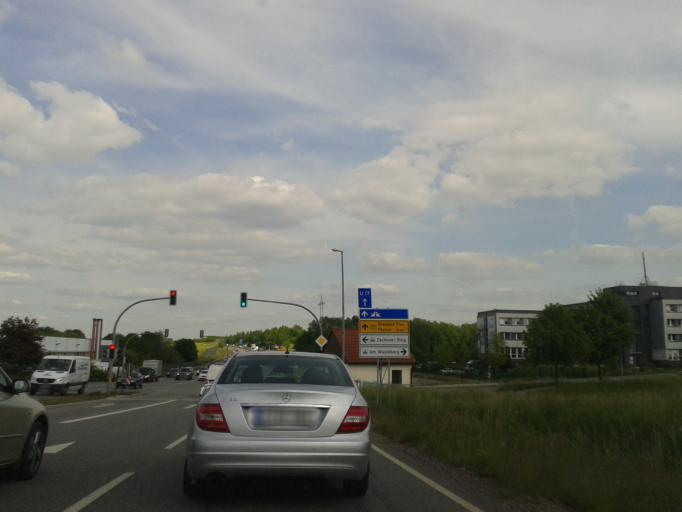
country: DE
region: Saxony
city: Tharandt
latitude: 51.0375
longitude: 13.5967
